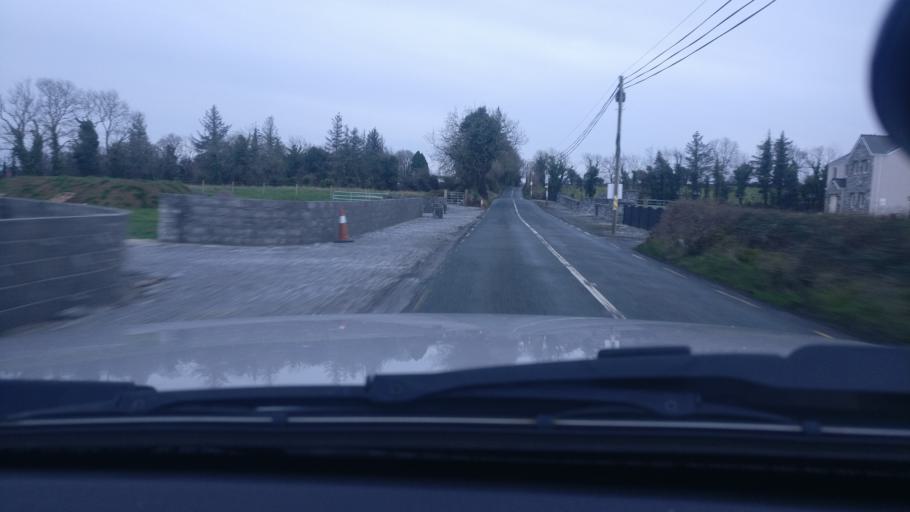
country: IE
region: Connaught
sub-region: County Galway
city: Loughrea
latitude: 53.1683
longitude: -8.5222
